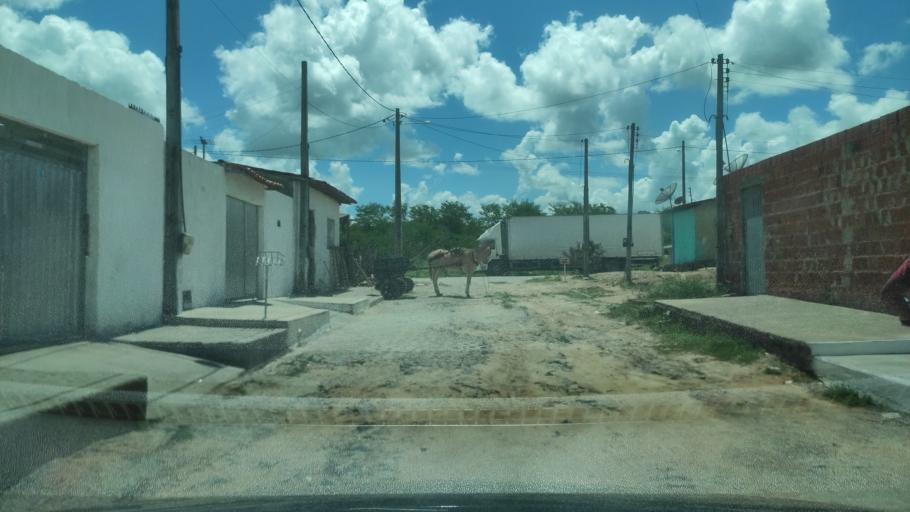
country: BR
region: Alagoas
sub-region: Uniao Dos Palmares
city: Uniao dos Palmares
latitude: -9.1446
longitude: -36.0019
